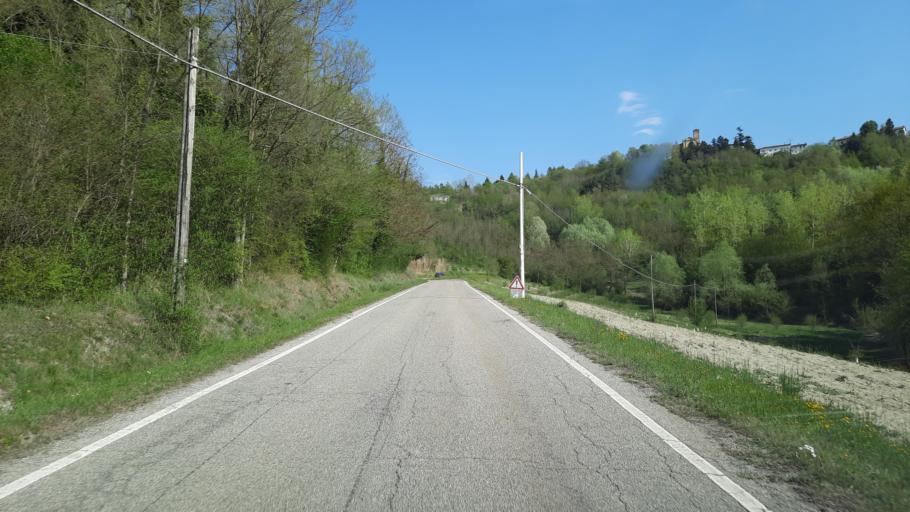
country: IT
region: Piedmont
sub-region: Provincia di Alessandria
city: Villamiroglio
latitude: 45.1385
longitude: 8.1657
